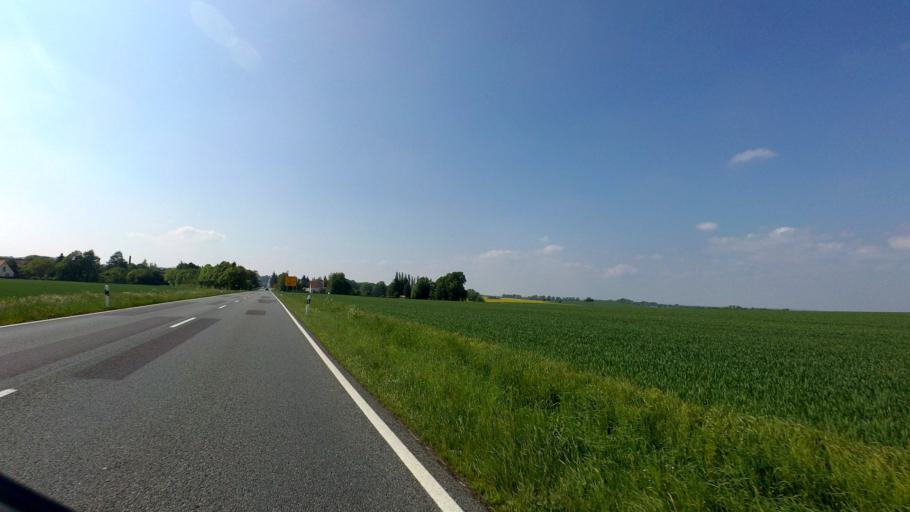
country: DE
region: Saxony
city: Hochkirch
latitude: 51.1362
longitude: 14.6008
